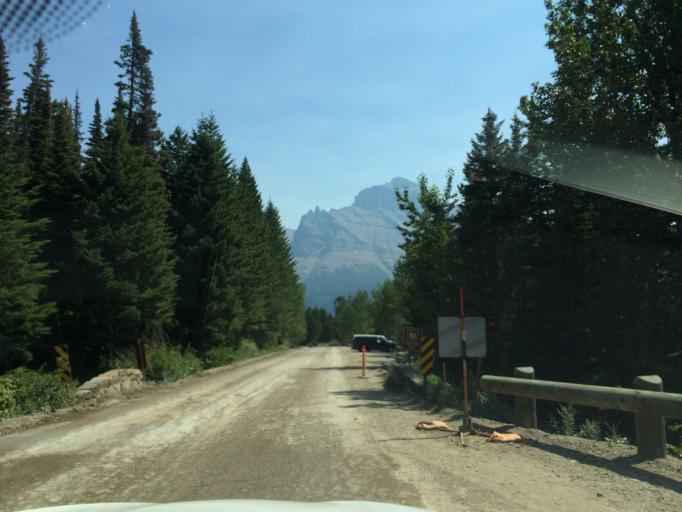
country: US
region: Montana
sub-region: Flathead County
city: Columbia Falls
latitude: 48.6783
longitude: -113.6537
